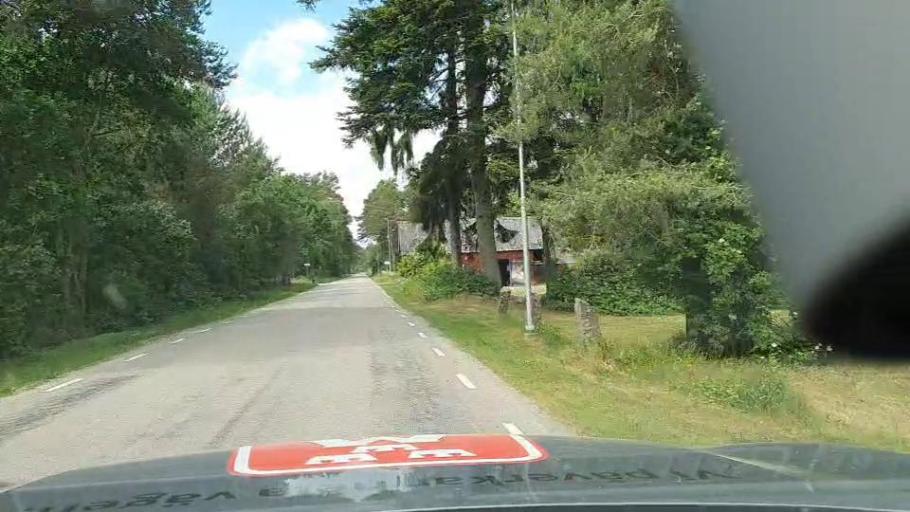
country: SE
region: Blekinge
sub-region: Karlshamns Kommun
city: Morrum
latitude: 56.0926
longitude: 14.6965
